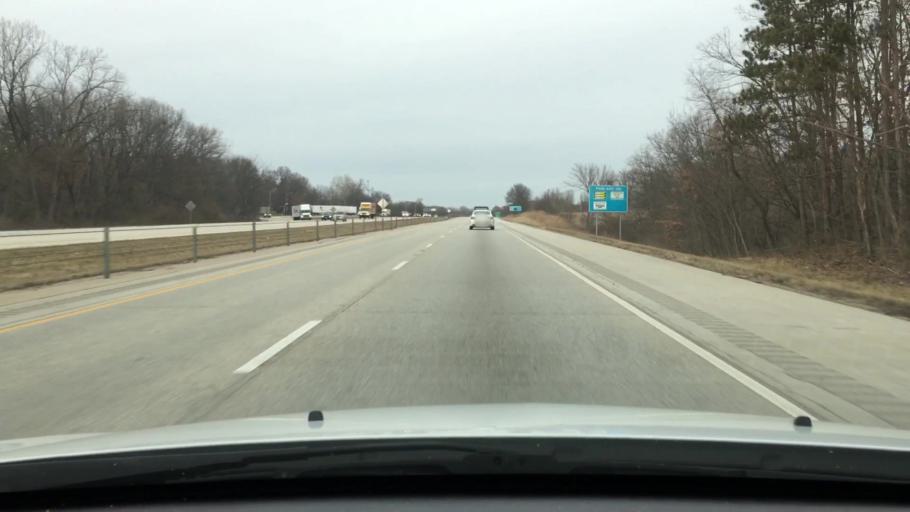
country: US
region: Illinois
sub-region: Sangamon County
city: Sherman
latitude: 39.8837
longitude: -89.5962
